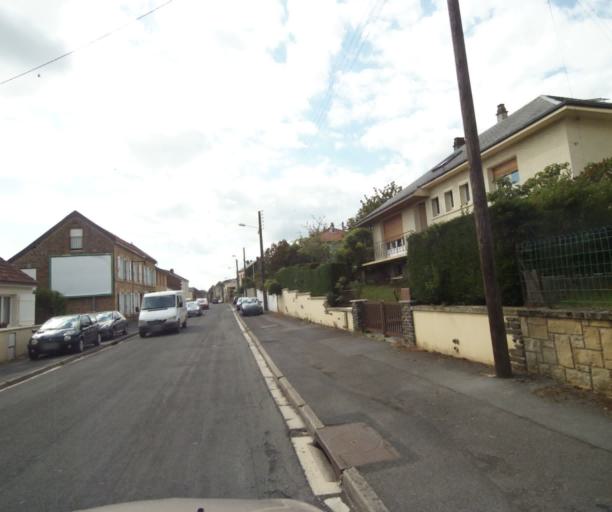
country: FR
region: Champagne-Ardenne
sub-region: Departement des Ardennes
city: Villers-Semeuse
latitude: 49.7580
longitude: 4.7430
